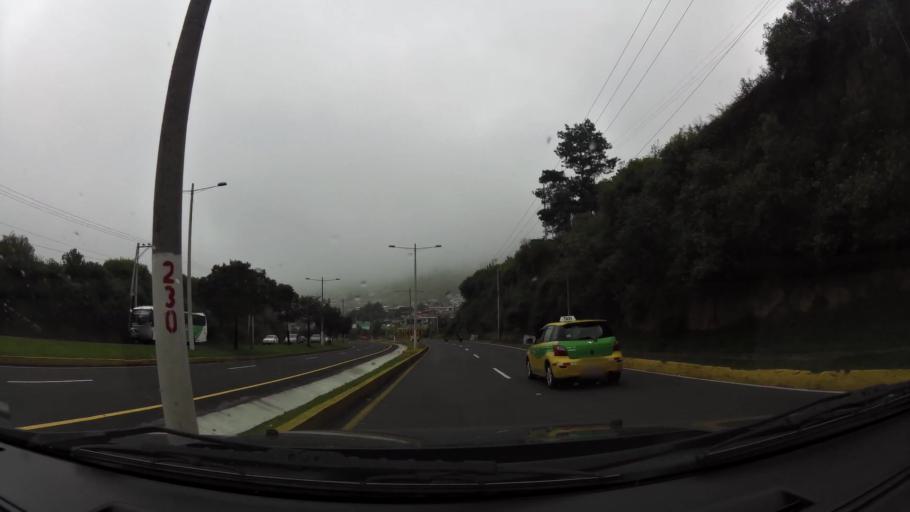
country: EC
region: Pichincha
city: Quito
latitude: -0.2703
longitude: -78.4892
